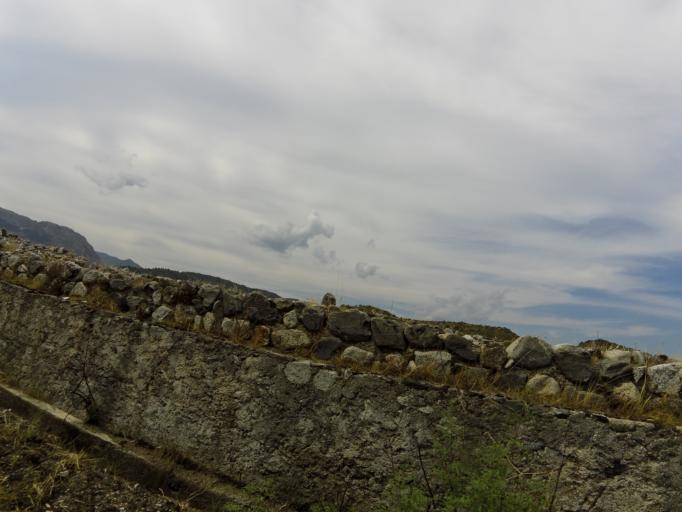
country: IT
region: Calabria
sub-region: Provincia di Reggio Calabria
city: Camini
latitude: 38.4612
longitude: 16.5085
